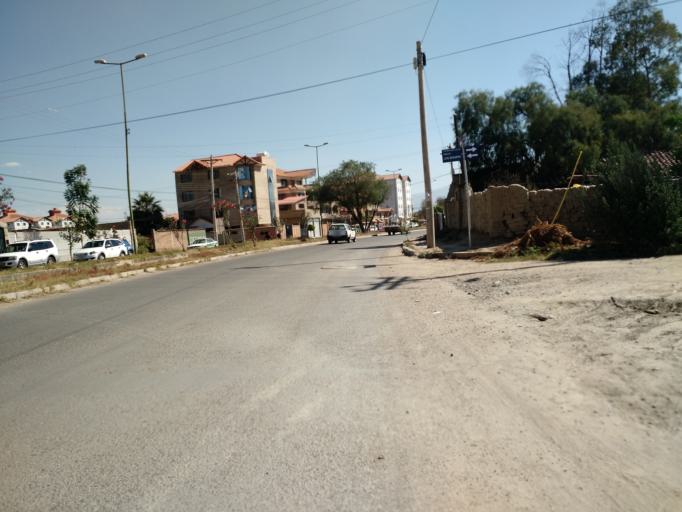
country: BO
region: Cochabamba
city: Cochabamba
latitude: -17.3866
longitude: -66.1931
